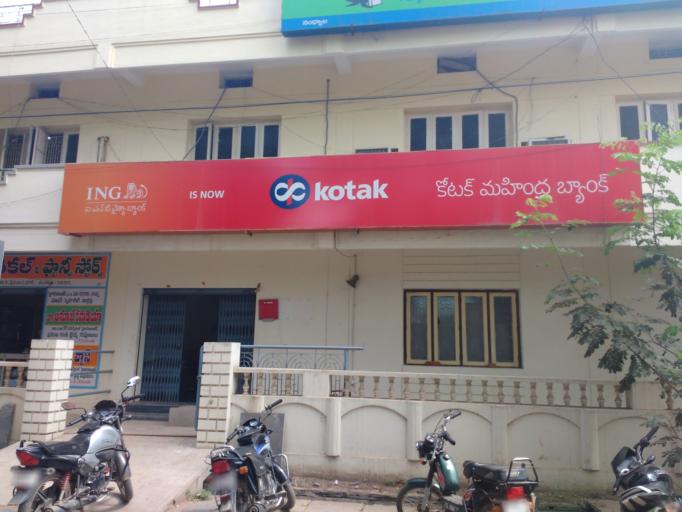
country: IN
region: Andhra Pradesh
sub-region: Kurnool
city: Nandyal
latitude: 15.4860
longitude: 78.4824
